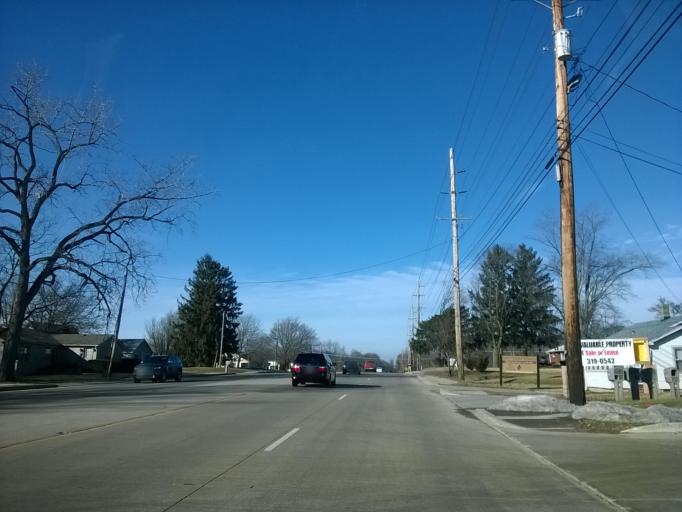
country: US
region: Indiana
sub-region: Boone County
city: Zionsville
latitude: 39.9599
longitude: -86.2460
